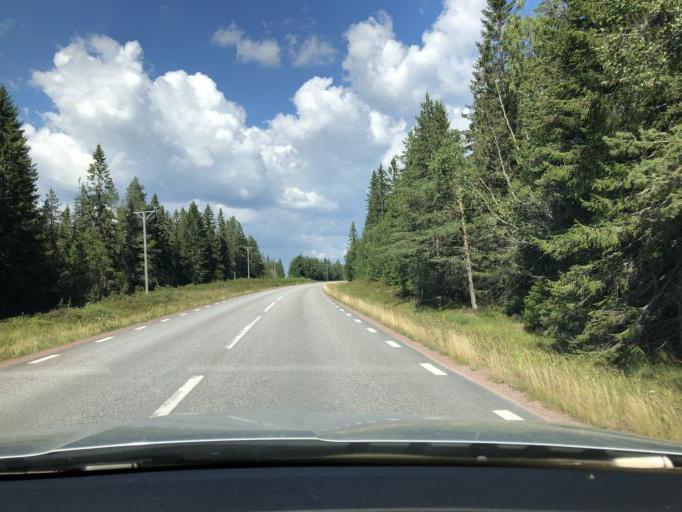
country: SE
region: Dalarna
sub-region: Orsa Kommun
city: Orsa
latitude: 61.3430
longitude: 14.7472
